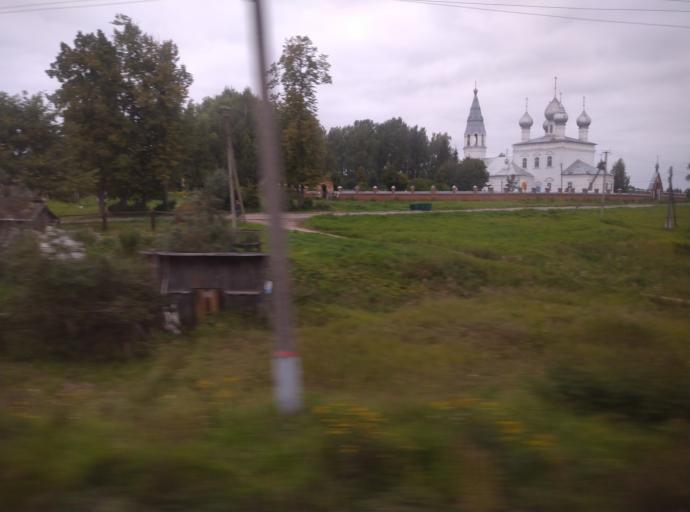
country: RU
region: Kostroma
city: Kosmynino
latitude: 57.5445
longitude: 40.7023
